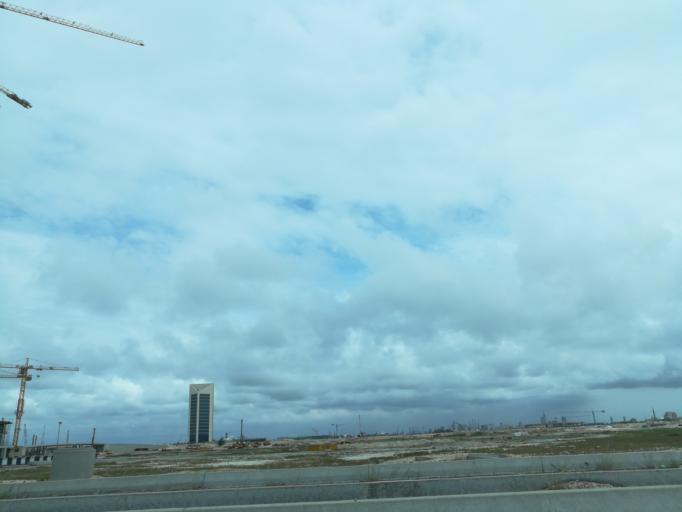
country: NG
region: Lagos
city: Lagos
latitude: 6.4024
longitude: 3.4086
